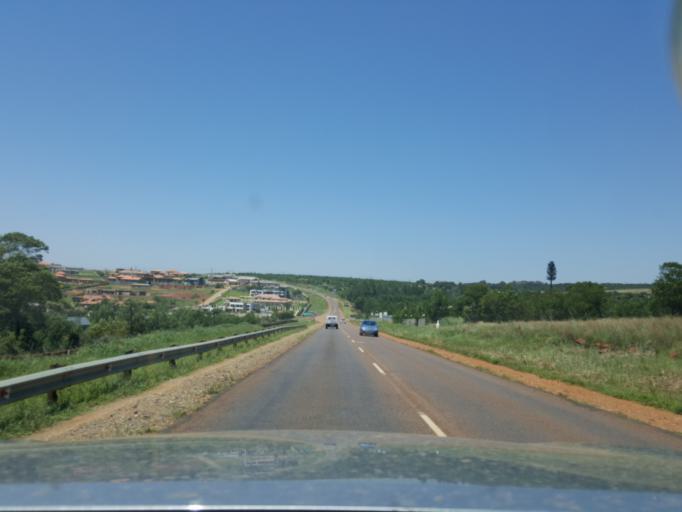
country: ZA
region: Gauteng
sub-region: City of Tshwane Metropolitan Municipality
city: Centurion
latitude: -25.8548
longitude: 28.3342
